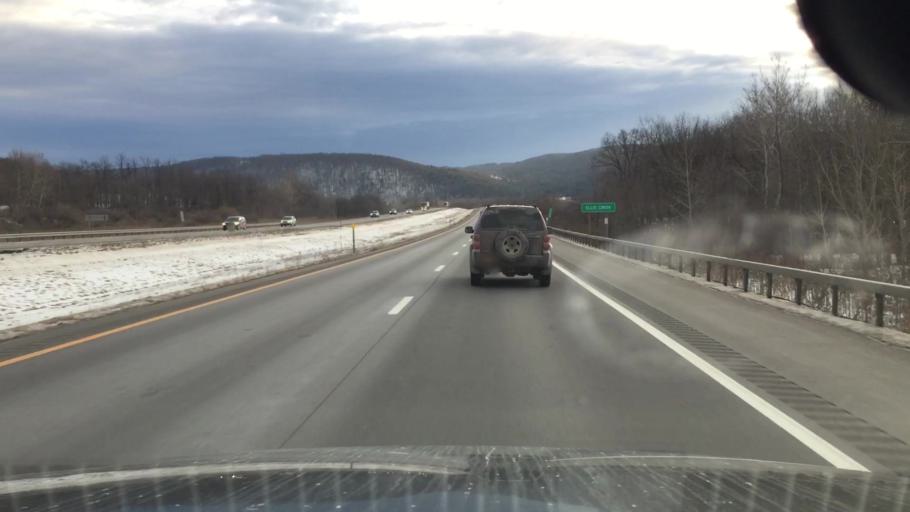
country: US
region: Pennsylvania
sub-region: Bradford County
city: Sayre
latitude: 42.0065
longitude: -76.4812
